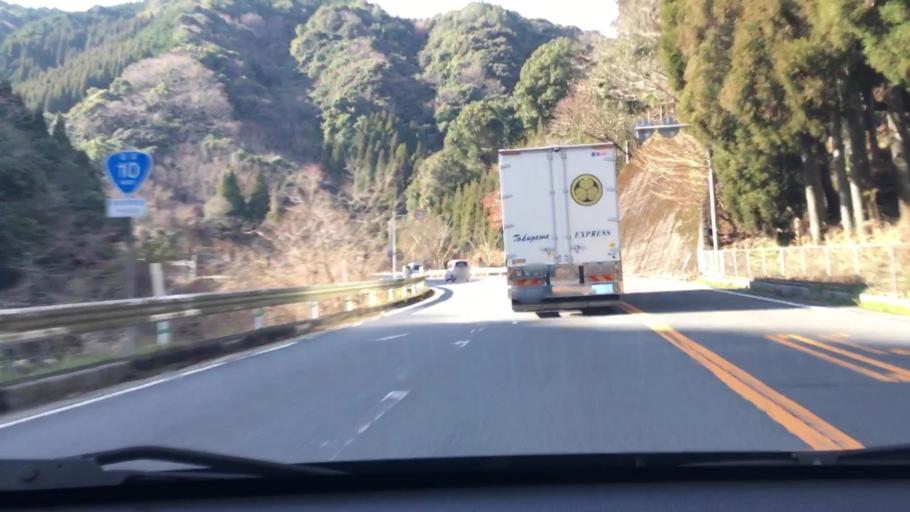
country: JP
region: Oita
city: Tsukumiura
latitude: 32.9988
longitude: 131.7830
